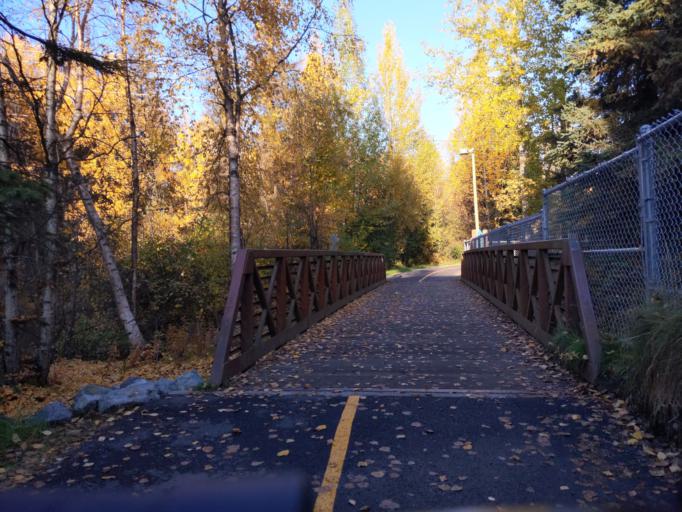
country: US
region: Alaska
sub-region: Anchorage Municipality
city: Anchorage
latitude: 61.1554
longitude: -149.8773
